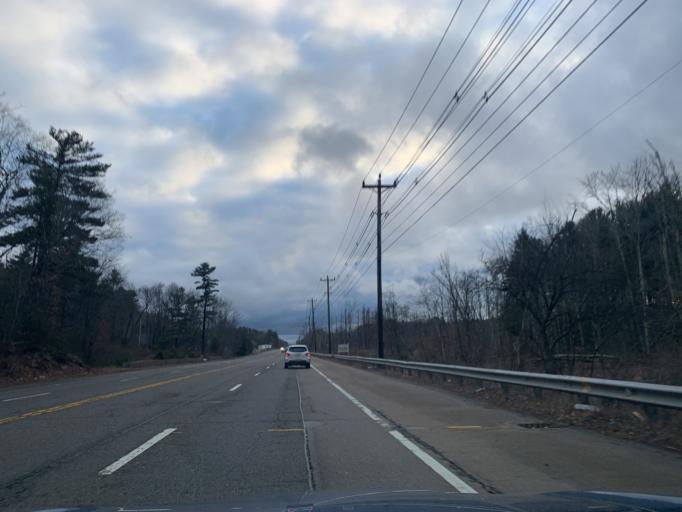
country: US
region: Massachusetts
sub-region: Norfolk County
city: Wrentham
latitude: 42.0625
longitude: -71.2952
